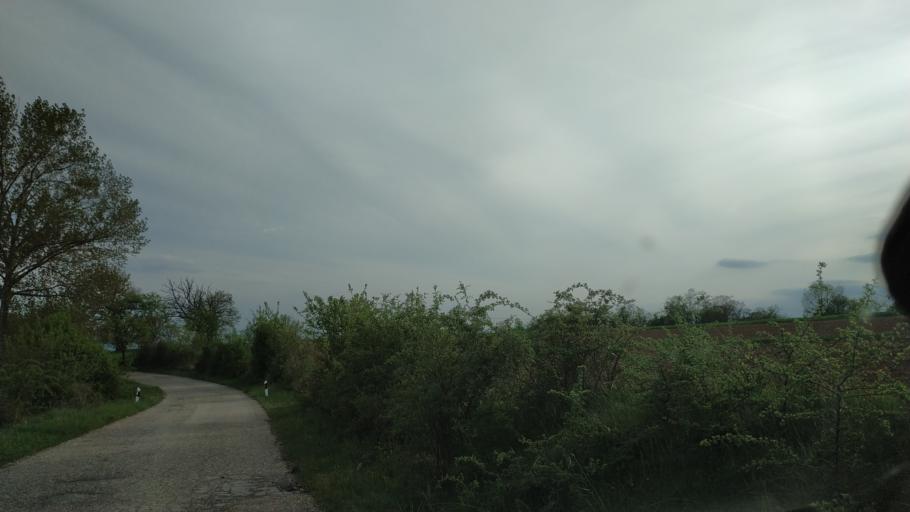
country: RS
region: Central Serbia
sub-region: Zajecarski Okrug
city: Soko Banja
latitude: 43.5363
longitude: 21.8787
